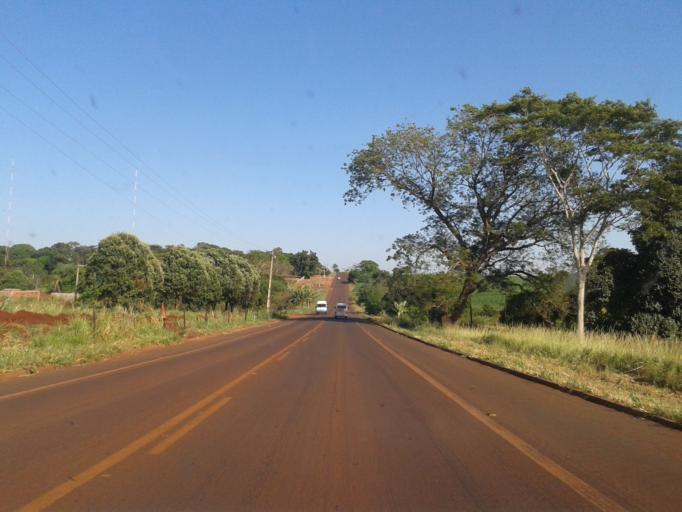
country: BR
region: Minas Gerais
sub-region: Capinopolis
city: Capinopolis
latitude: -18.6848
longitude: -49.5855
